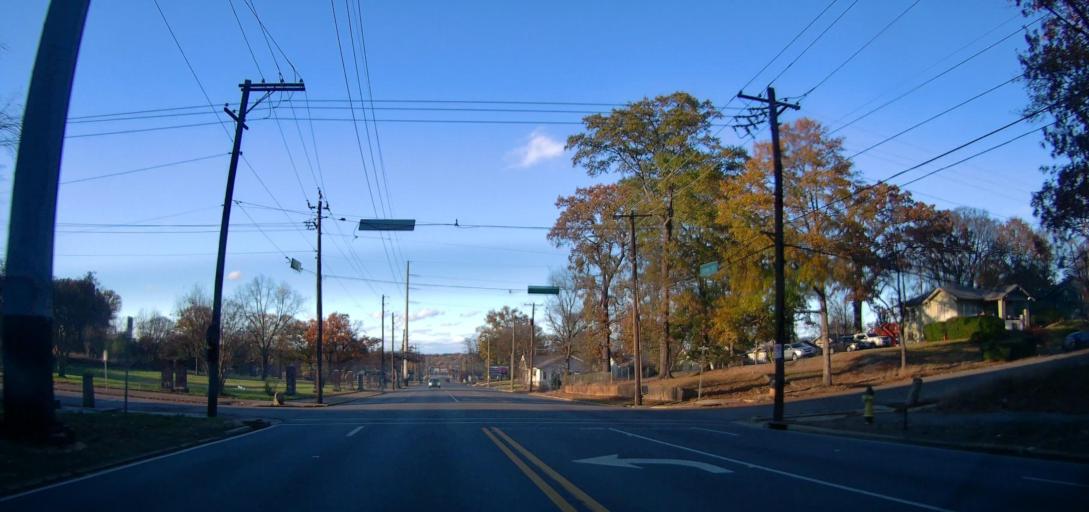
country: US
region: Alabama
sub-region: Jefferson County
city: Birmingham
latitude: 33.5377
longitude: -86.8105
